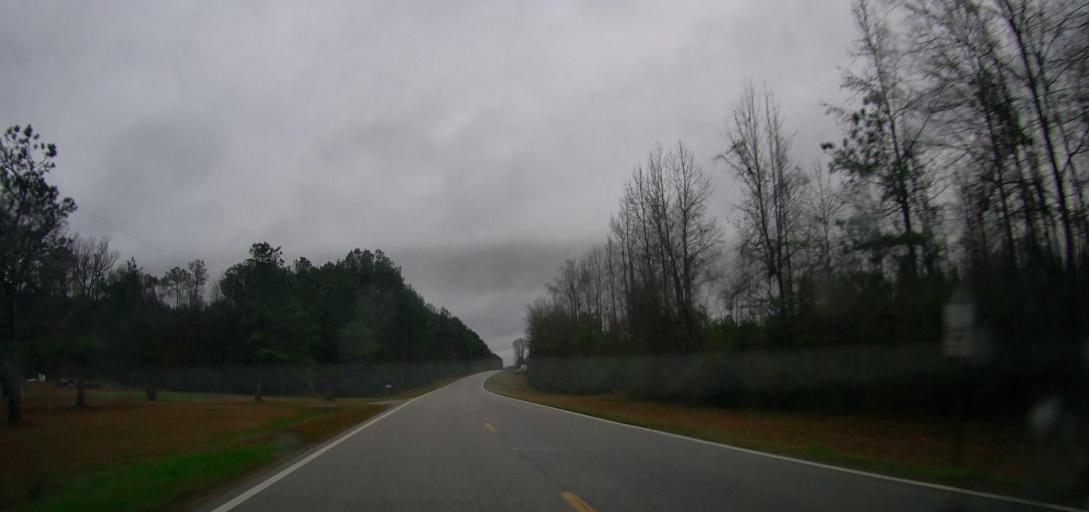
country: US
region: Alabama
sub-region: Bibb County
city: Centreville
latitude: 32.9184
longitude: -87.0302
